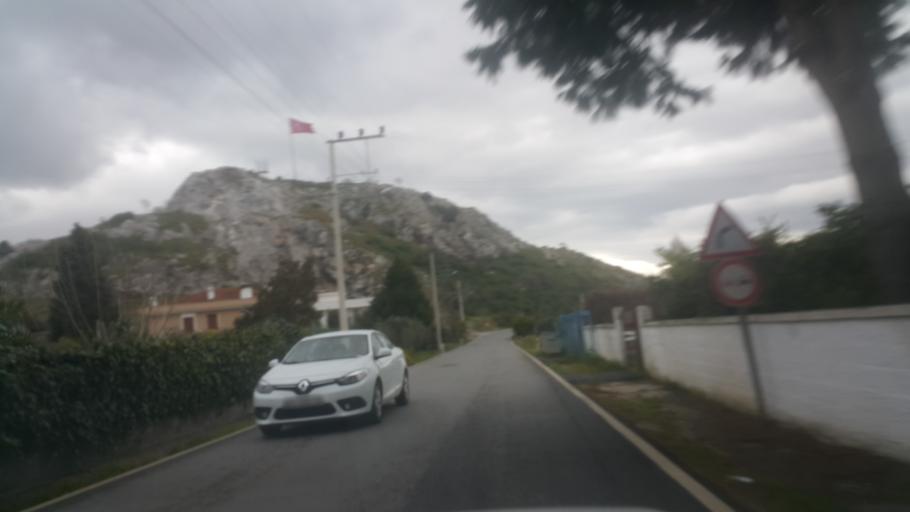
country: TR
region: Izmir
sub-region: Seferihisar
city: Seferhisar
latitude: 38.1905
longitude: 26.8044
